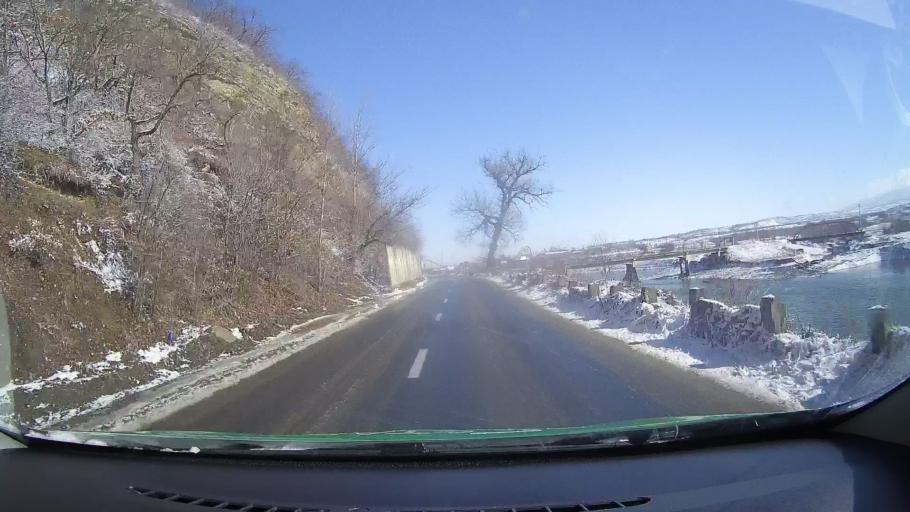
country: RO
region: Sibiu
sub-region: Comuna Turnu Rosu
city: Turnu Rosu
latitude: 45.6682
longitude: 24.3136
